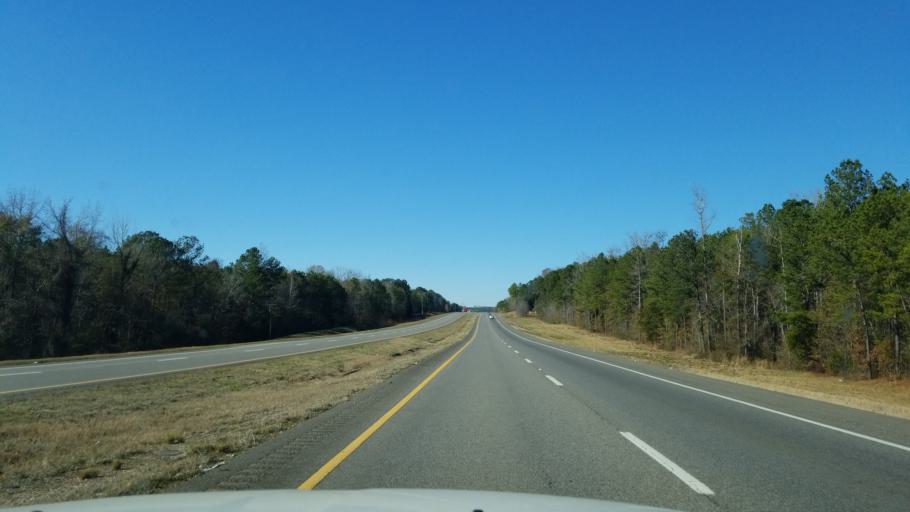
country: US
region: Alabama
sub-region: Tuscaloosa County
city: Northport
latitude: 33.2540
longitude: -87.6903
